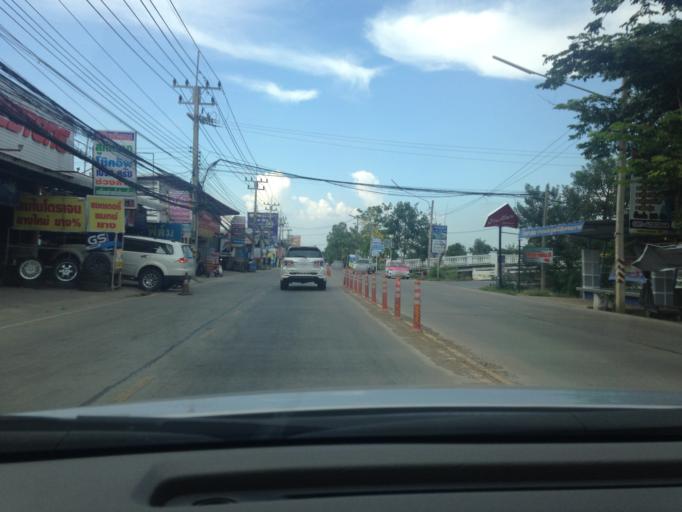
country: TH
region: Pathum Thani
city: Khlong Luang
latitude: 14.0573
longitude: 100.6635
